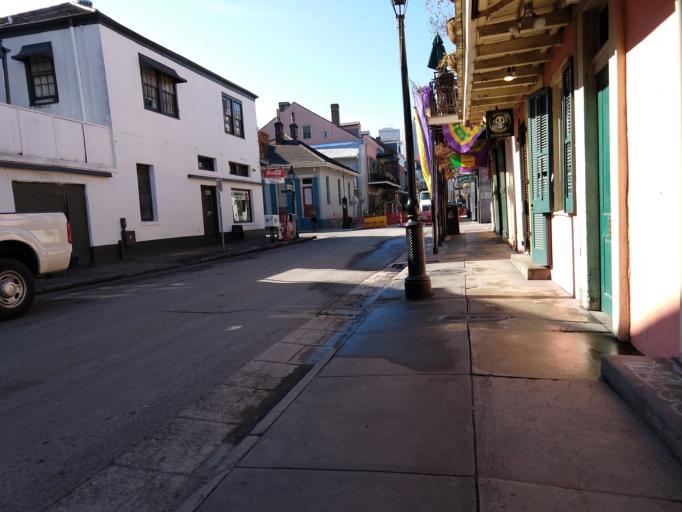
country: US
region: Louisiana
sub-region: Orleans Parish
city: New Orleans
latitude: 29.9605
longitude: -90.0640
